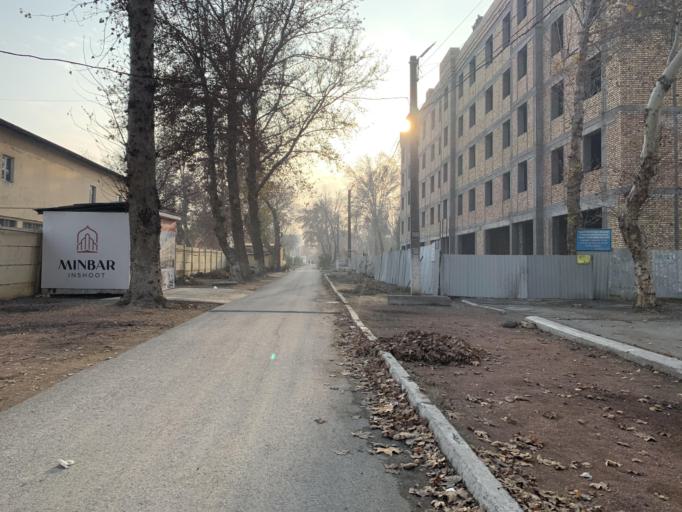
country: UZ
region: Fergana
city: Qo`qon
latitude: 40.5449
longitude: 70.9243
